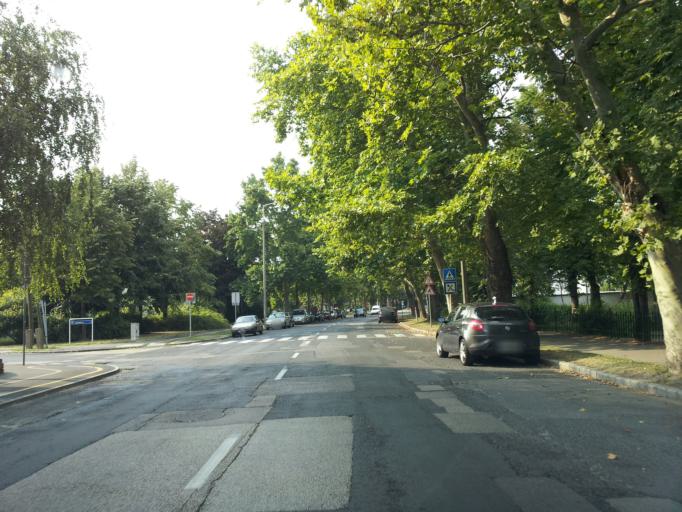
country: HU
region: Gyor-Moson-Sopron
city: Gyor
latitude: 47.6711
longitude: 17.6456
